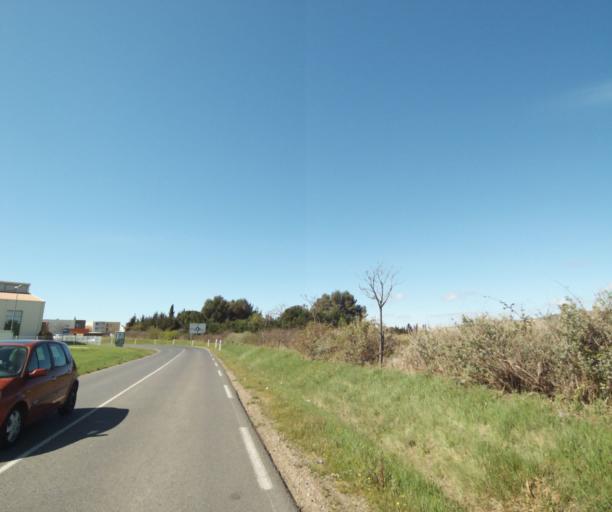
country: FR
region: Languedoc-Roussillon
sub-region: Departement de l'Herault
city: Villeneuve-les-Maguelone
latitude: 43.5346
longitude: 3.8525
